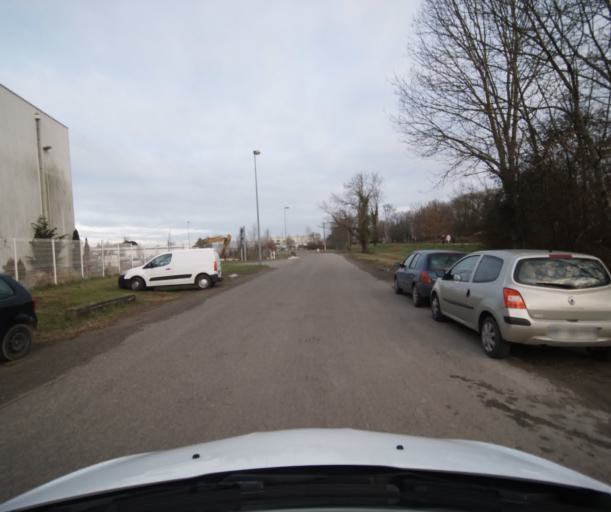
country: FR
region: Midi-Pyrenees
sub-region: Departement du Tarn-et-Garonne
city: Castelsarrasin
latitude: 44.0568
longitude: 1.1043
